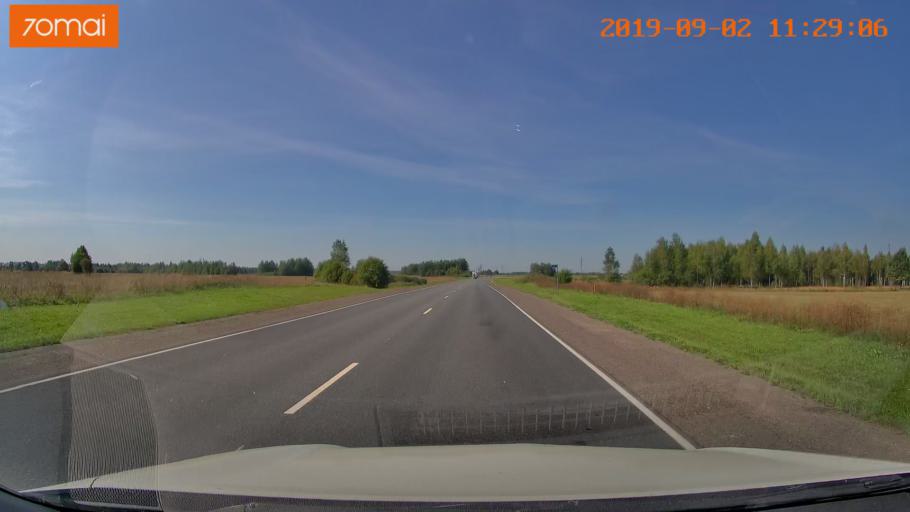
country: RU
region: Smolensk
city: Roslavl'
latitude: 53.9910
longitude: 32.8695
